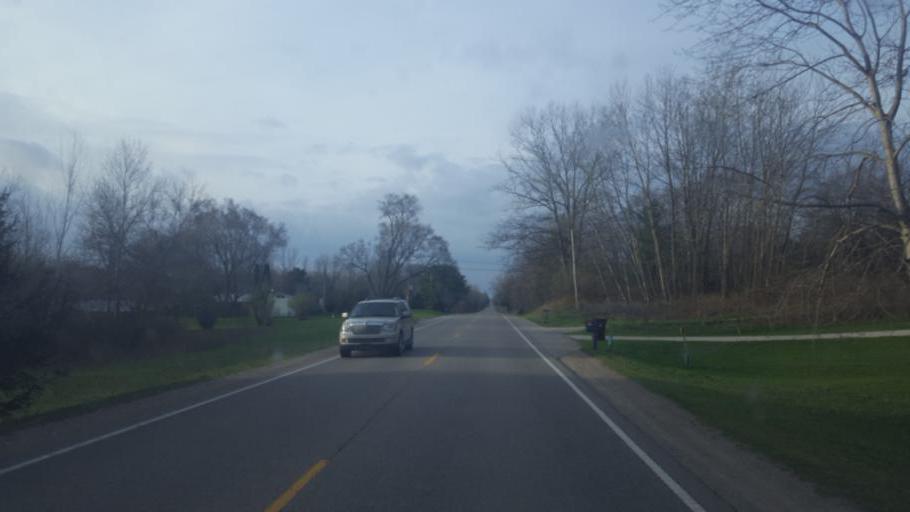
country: US
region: Michigan
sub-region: Isabella County
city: Lake Isabella
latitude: 43.5883
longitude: -84.9076
